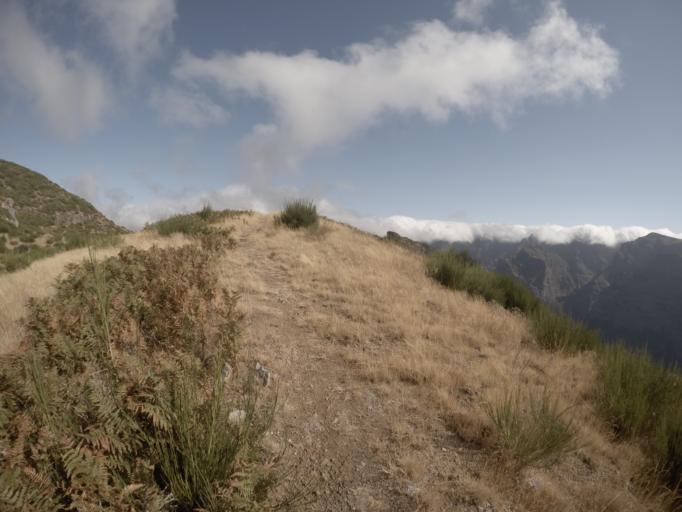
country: PT
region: Madeira
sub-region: Camara de Lobos
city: Curral das Freiras
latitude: 32.7131
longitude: -16.9895
